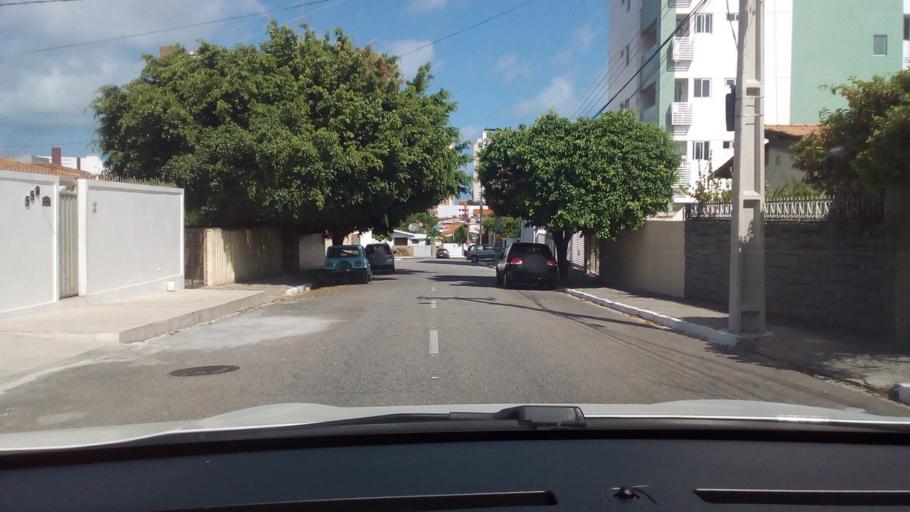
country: BR
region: Paraiba
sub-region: Joao Pessoa
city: Joao Pessoa
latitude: -7.1229
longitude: -34.8397
